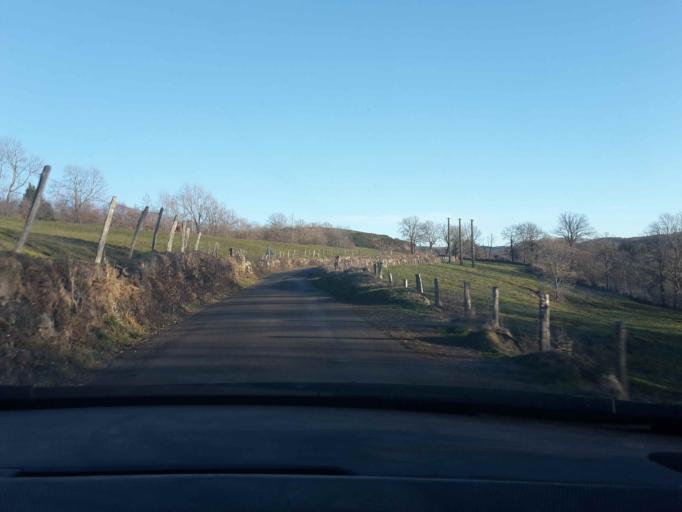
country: FR
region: Auvergne
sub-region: Departement du Cantal
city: Ydes
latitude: 45.2393
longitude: 2.5436
